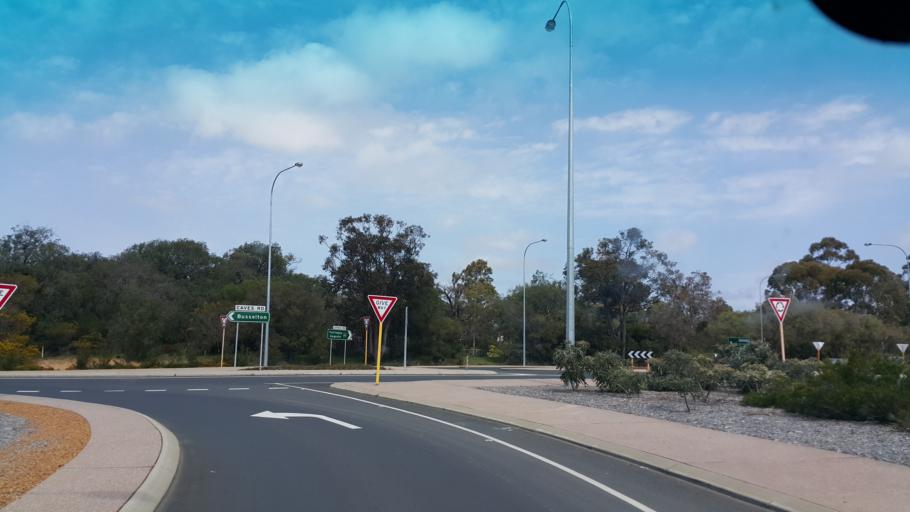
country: AU
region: Western Australia
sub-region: Busselton
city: Dunsborough
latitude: -33.6172
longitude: 115.1014
